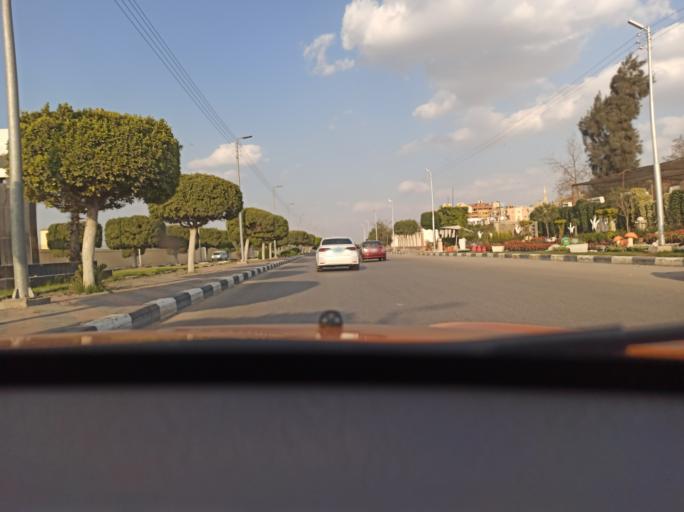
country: EG
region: Al Isma'iliyah
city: Ismailia
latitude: 30.6144
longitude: 32.2499
